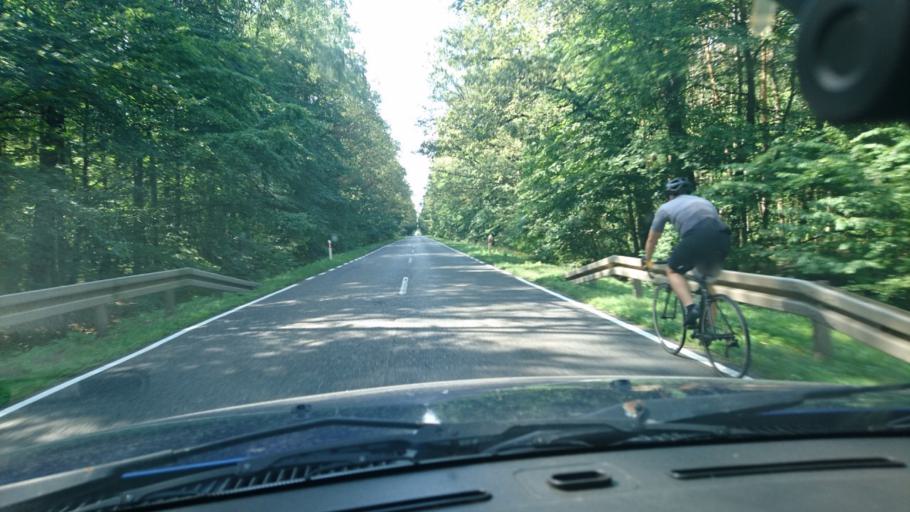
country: PL
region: Greater Poland Voivodeship
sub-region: Powiat ostrowski
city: Odolanow
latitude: 51.5968
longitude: 17.6110
